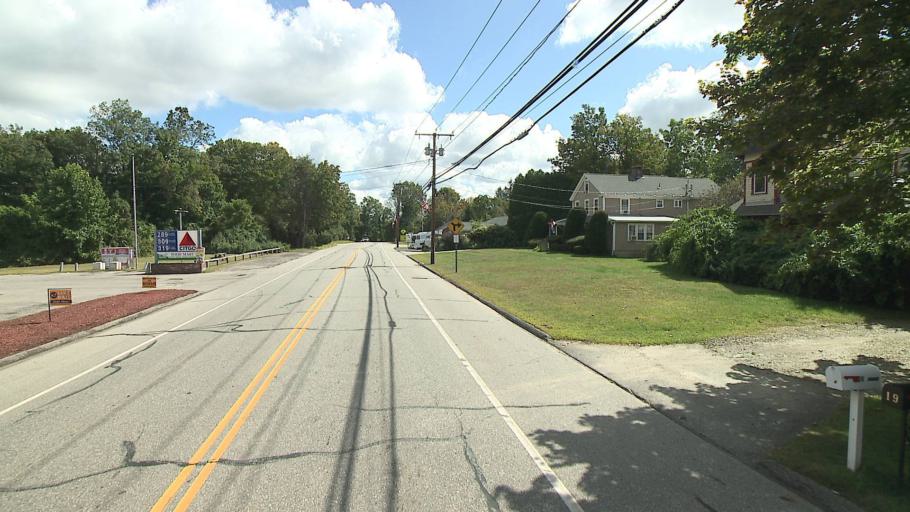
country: US
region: Connecticut
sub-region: Windham County
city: South Woodstock
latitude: 41.8977
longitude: -71.9601
